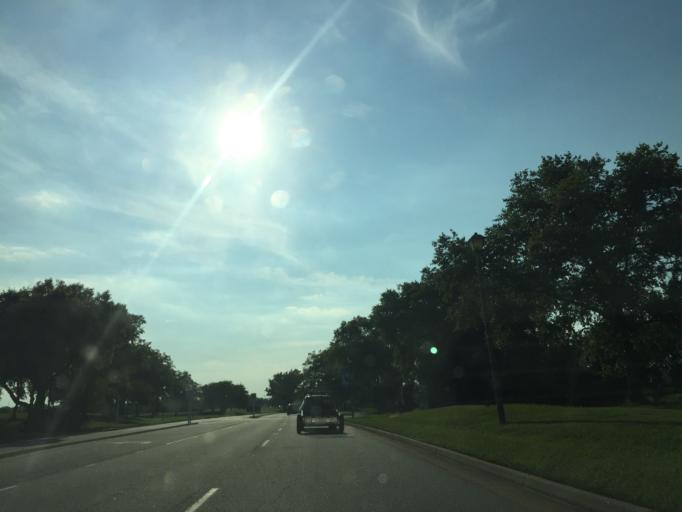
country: US
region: Virginia
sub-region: York County
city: Yorktown
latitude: 37.1187
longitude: -76.4987
